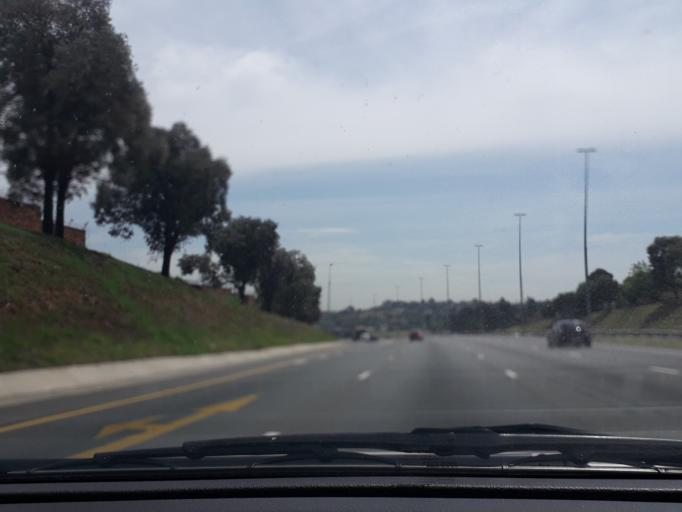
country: ZA
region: Gauteng
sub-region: City of Johannesburg Metropolitan Municipality
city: Roodepoort
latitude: -26.1703
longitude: 27.9426
